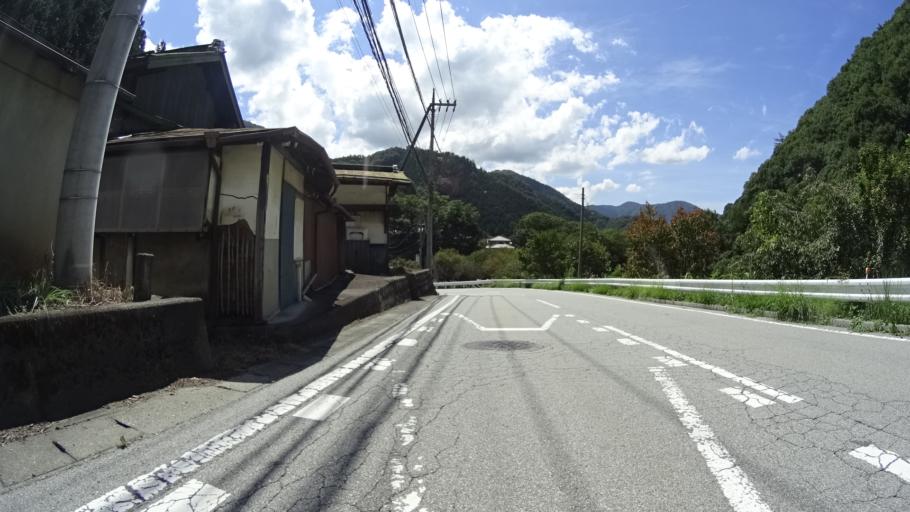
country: JP
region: Yamanashi
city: Enzan
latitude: 35.6416
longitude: 138.8024
